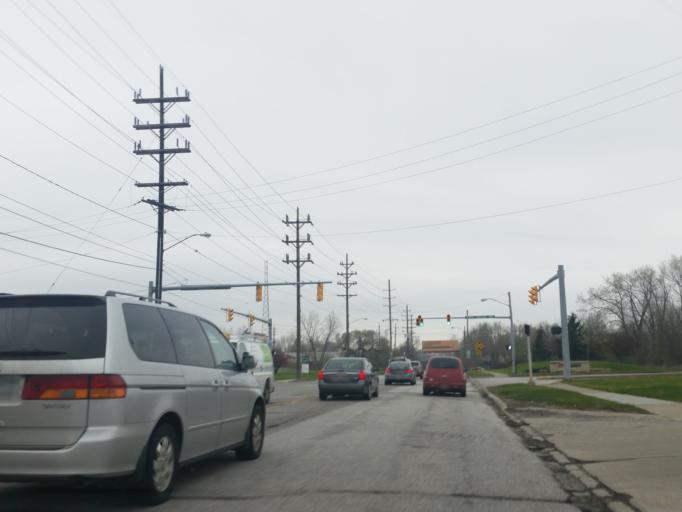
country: US
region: Ohio
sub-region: Cuyahoga County
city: Brooklyn
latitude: 41.4424
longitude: -81.7617
